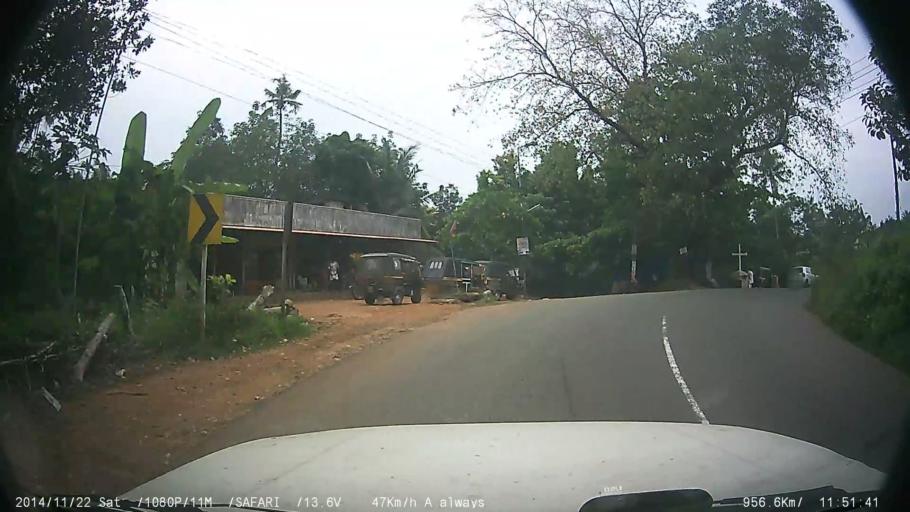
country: IN
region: Kerala
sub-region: Kottayam
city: Palackattumala
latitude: 9.8175
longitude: 76.5870
